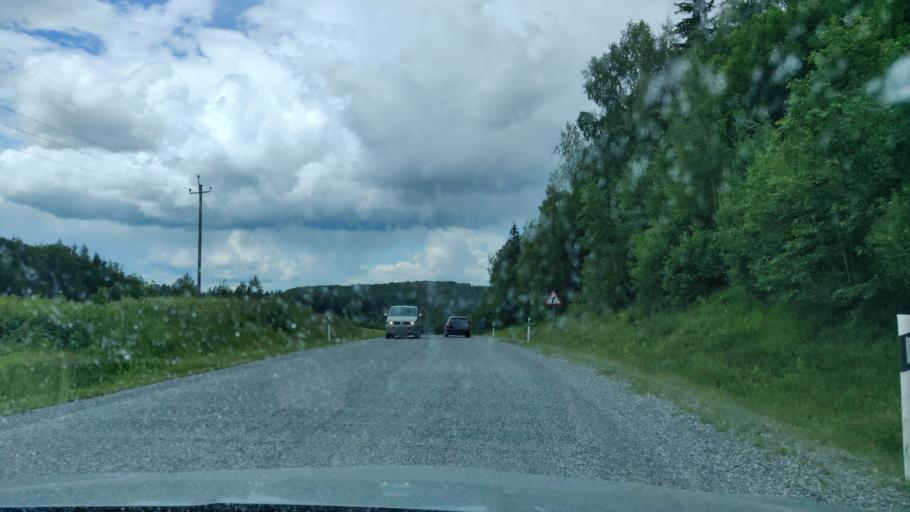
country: EE
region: Vorumaa
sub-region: Antsla vald
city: Vana-Antsla
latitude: 58.0378
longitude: 26.5584
